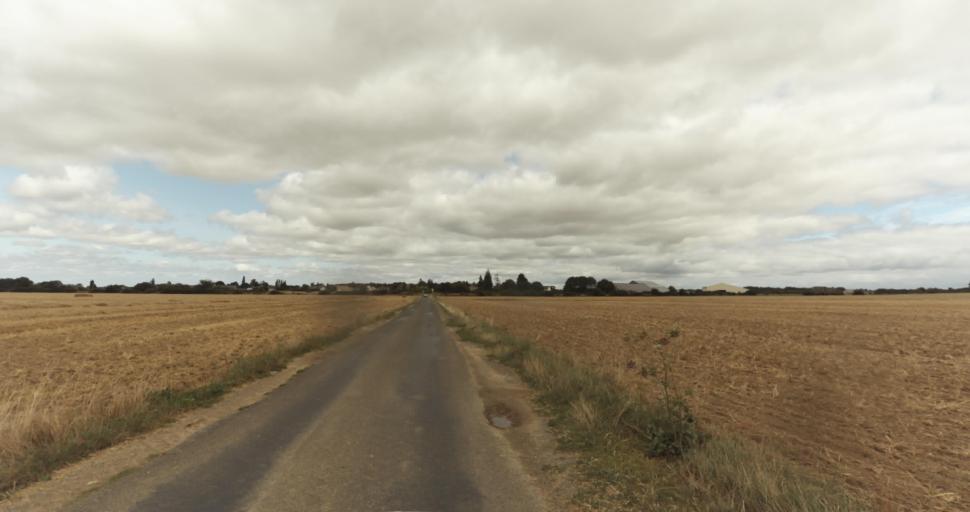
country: FR
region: Haute-Normandie
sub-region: Departement de l'Eure
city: Marcilly-sur-Eure
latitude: 48.9166
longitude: 1.2454
